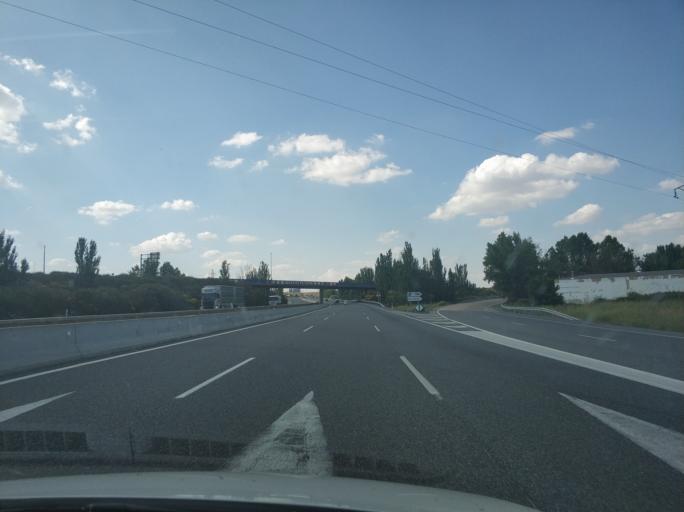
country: ES
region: Castille and Leon
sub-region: Provincia de Zamora
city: Benavente
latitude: 42.0148
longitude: -5.6652
